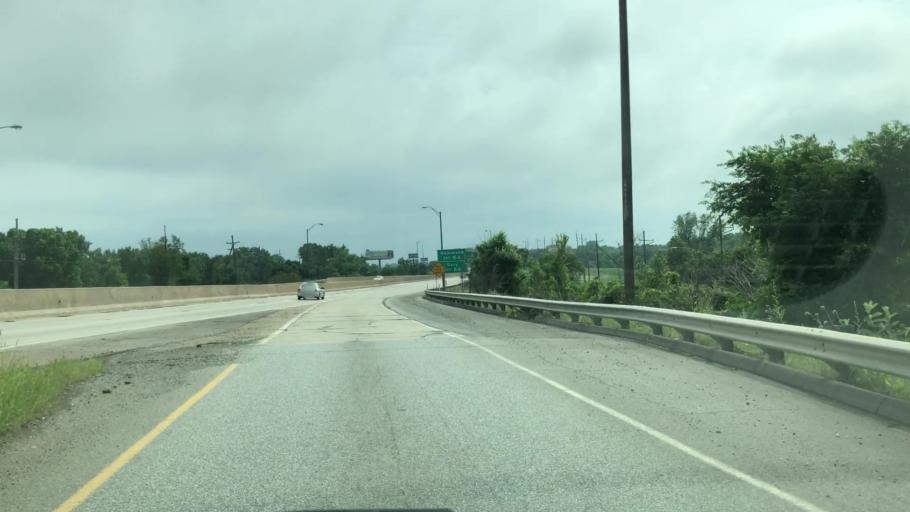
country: US
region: Indiana
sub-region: Lake County
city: East Chicago
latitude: 41.6152
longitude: -87.4322
